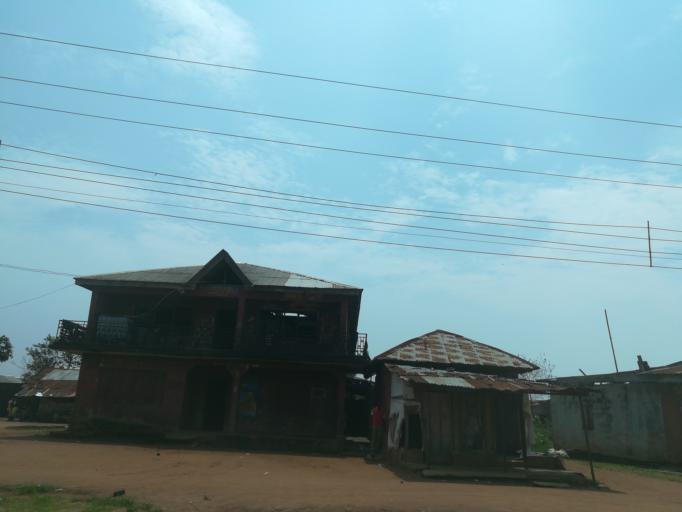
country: NG
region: Lagos
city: Ikorodu
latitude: 6.5765
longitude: 3.6289
